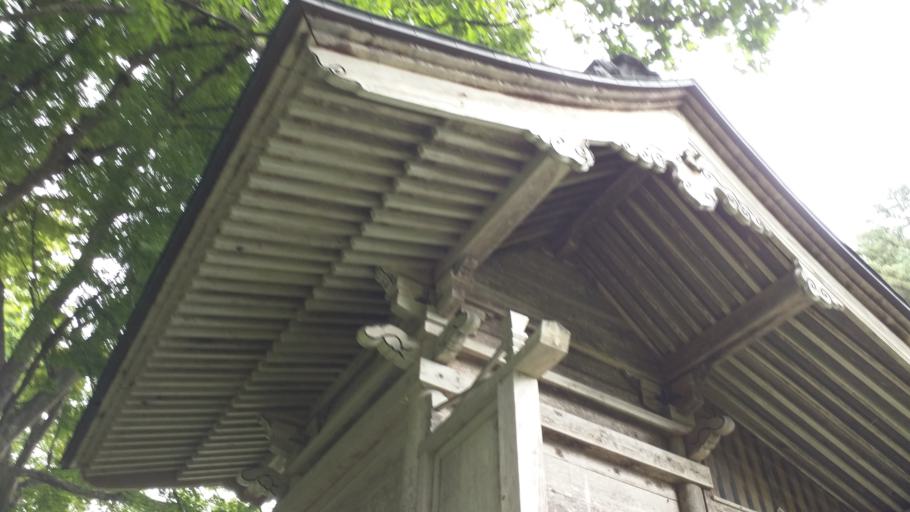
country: JP
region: Fukushima
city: Kitakata
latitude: 37.6304
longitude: 139.8320
